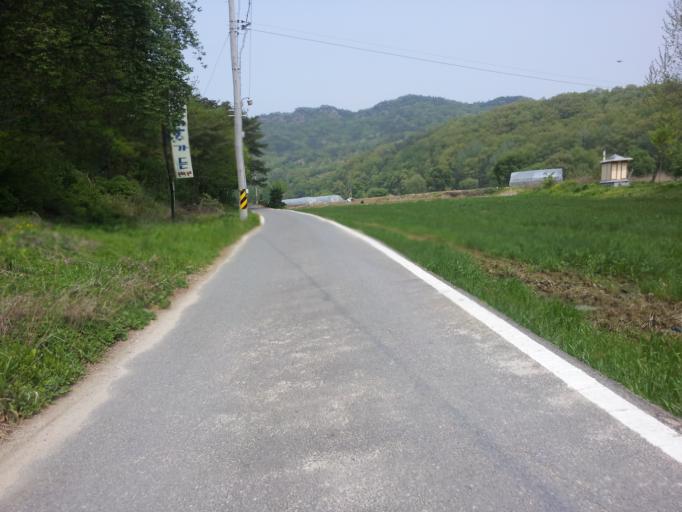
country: KR
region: Daejeon
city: Daejeon
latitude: 36.2765
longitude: 127.3429
